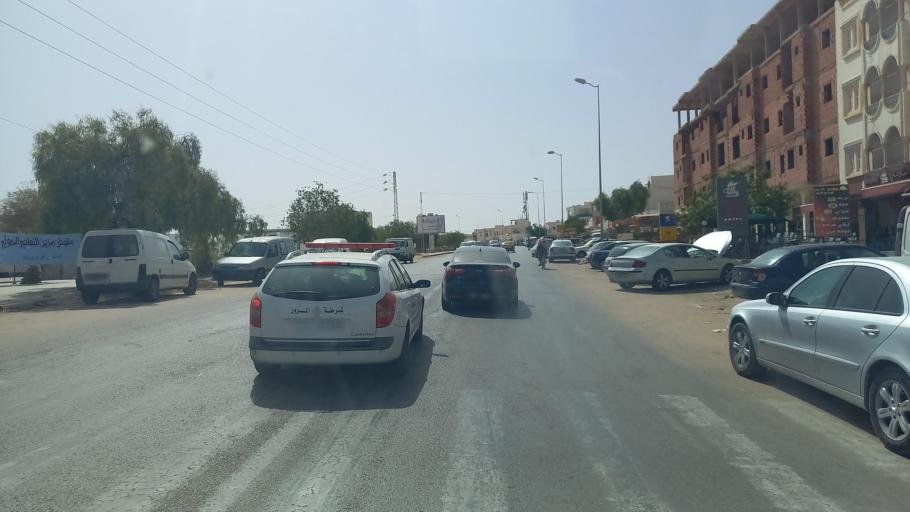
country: TN
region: Madanin
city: Medenine
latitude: 33.3436
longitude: 10.5027
